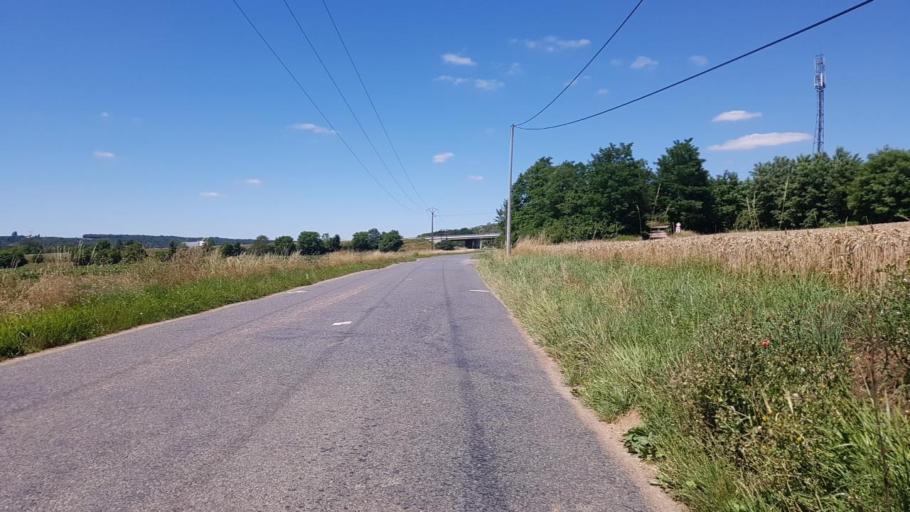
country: FR
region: Ile-de-France
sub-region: Departement de Seine-et-Marne
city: Sammeron
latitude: 48.9587
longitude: 3.0559
